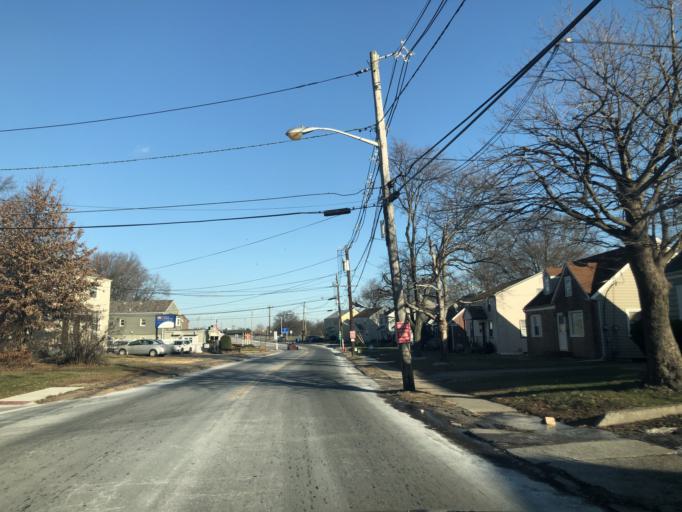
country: US
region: New Jersey
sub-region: Middlesex County
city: Fords
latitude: 40.5332
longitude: -74.3048
